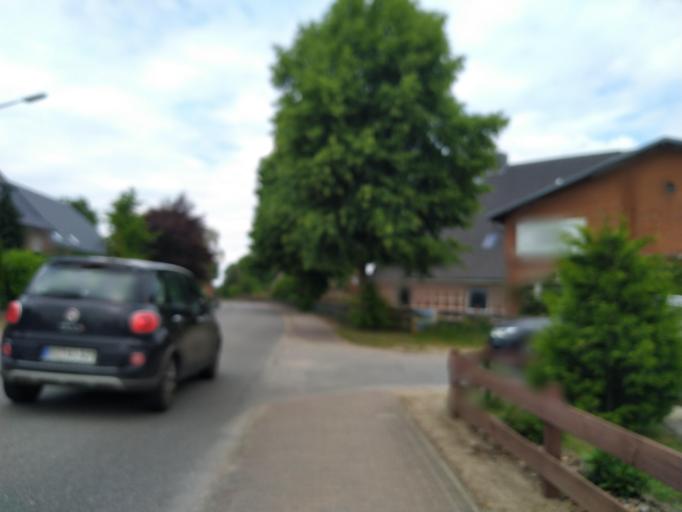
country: DE
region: Schleswig-Holstein
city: Klempau
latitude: 53.7634
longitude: 10.6625
